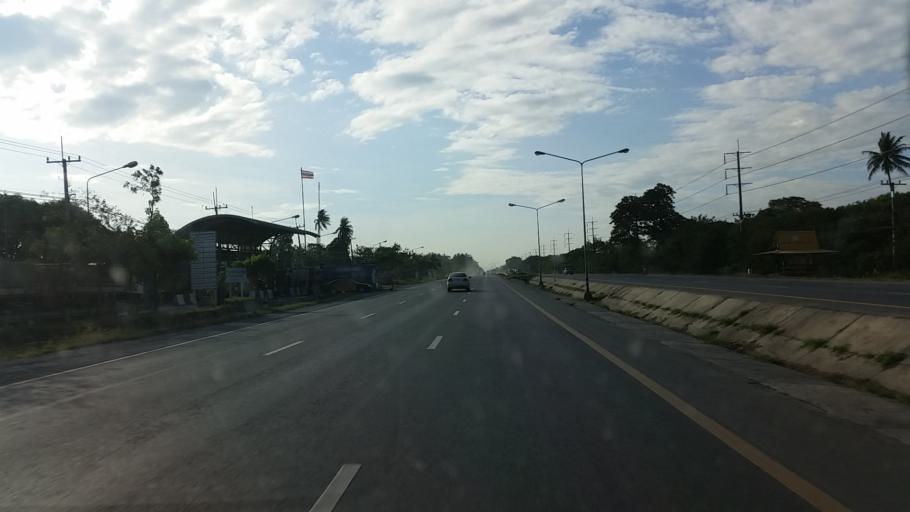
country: TH
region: Sara Buri
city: Chaloem Phra Kiat
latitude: 14.6473
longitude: 100.8853
